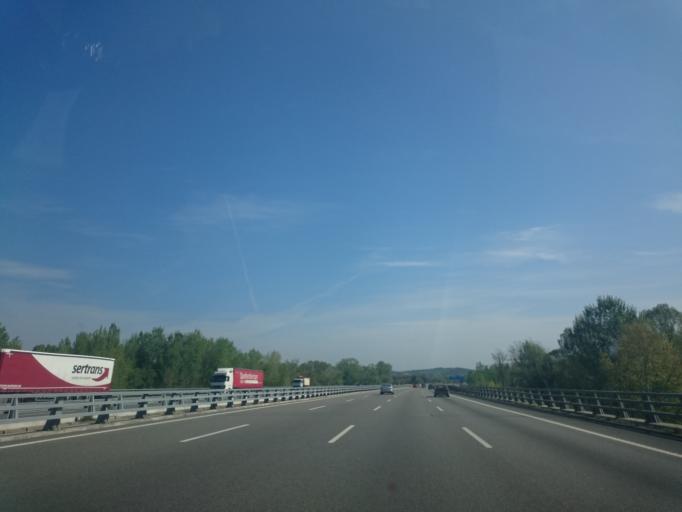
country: ES
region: Catalonia
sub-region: Provincia de Girona
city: Salt
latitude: 41.9826
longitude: 2.7816
